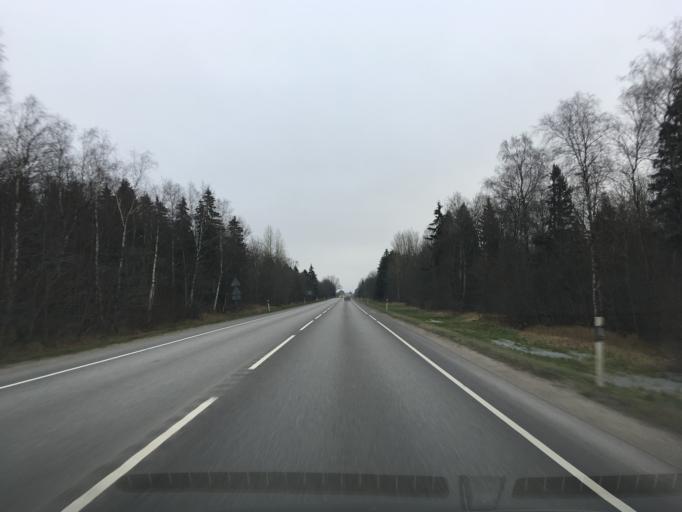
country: EE
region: Ida-Virumaa
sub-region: Kohtla-Jaerve linn
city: Kohtla-Jarve
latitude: 59.4182
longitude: 27.2871
